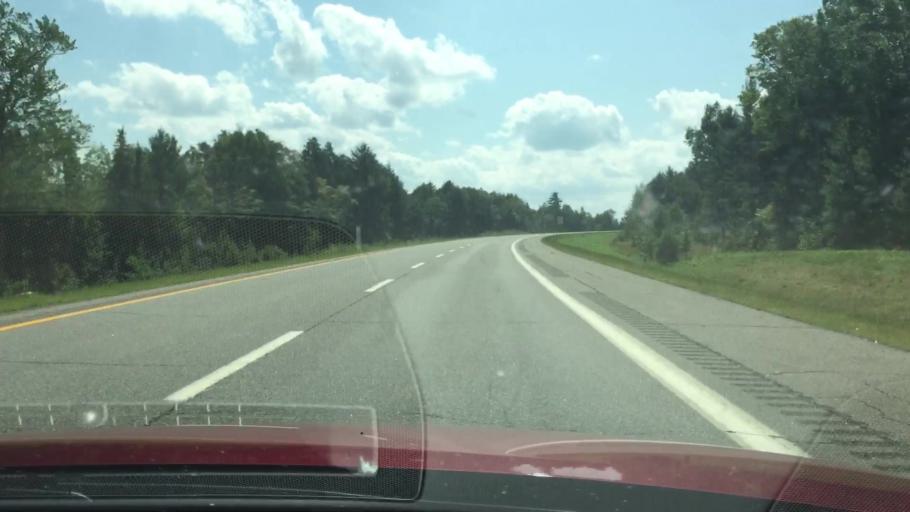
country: US
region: Maine
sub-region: Penobscot County
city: Lincoln
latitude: 45.3550
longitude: -68.6072
